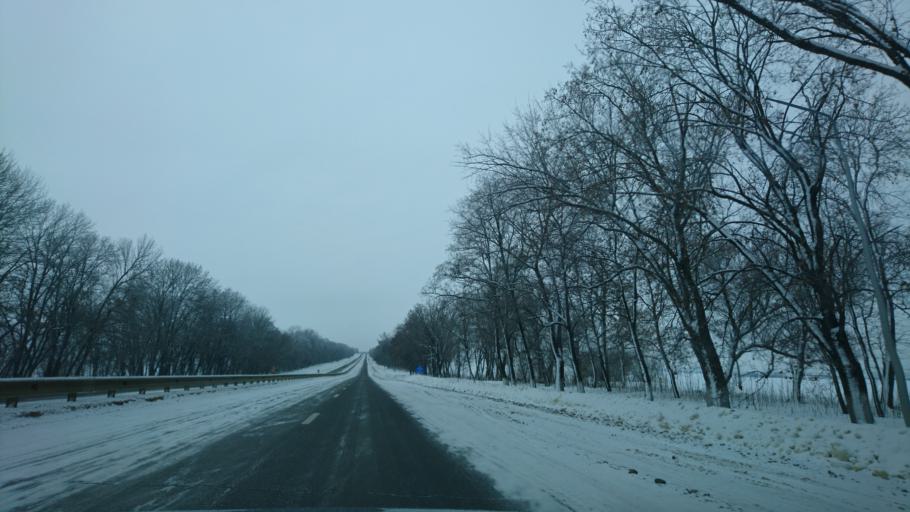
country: RU
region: Belgorod
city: Mayskiy
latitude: 50.4331
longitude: 36.3876
